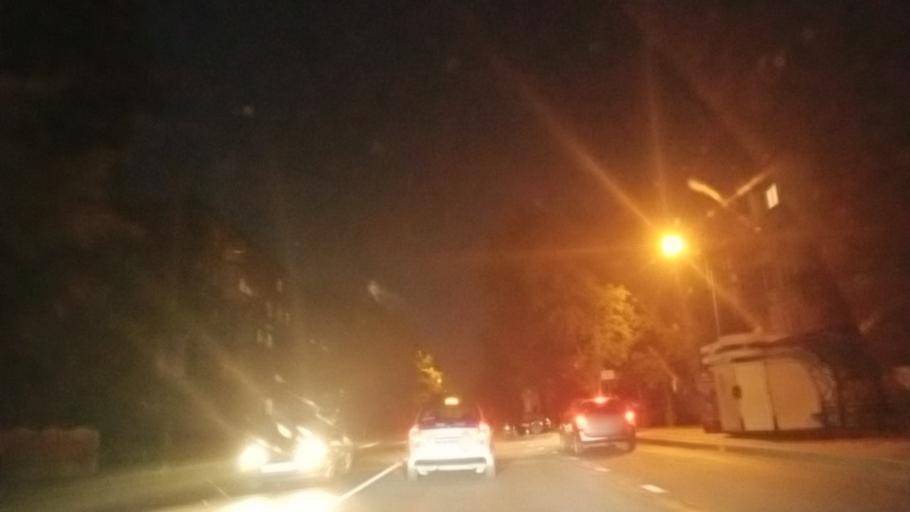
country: BY
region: Brest
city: Brest
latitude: 52.0588
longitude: 23.7275
